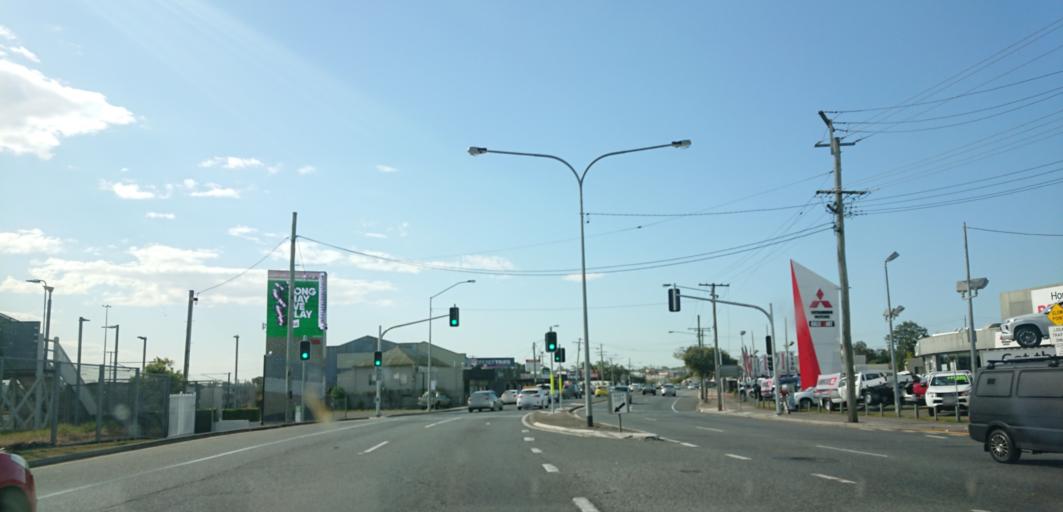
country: AU
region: Queensland
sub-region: Brisbane
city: Rocklea
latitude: -27.5363
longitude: 153.0142
